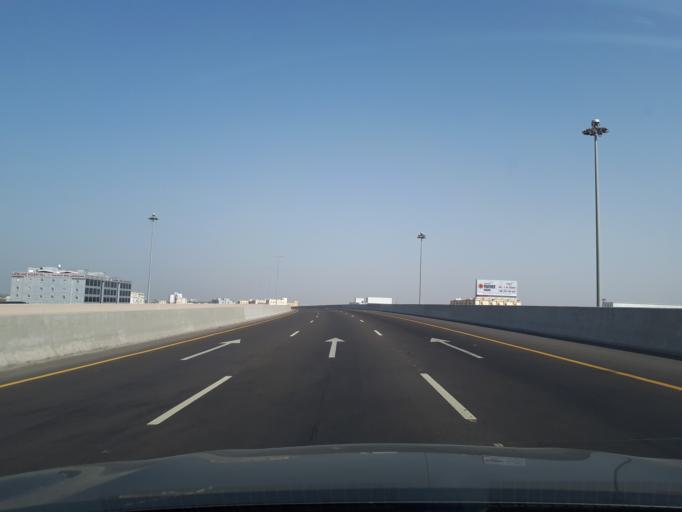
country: OM
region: Al Batinah
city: Al Liwa'
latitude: 24.4254
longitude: 56.6099
